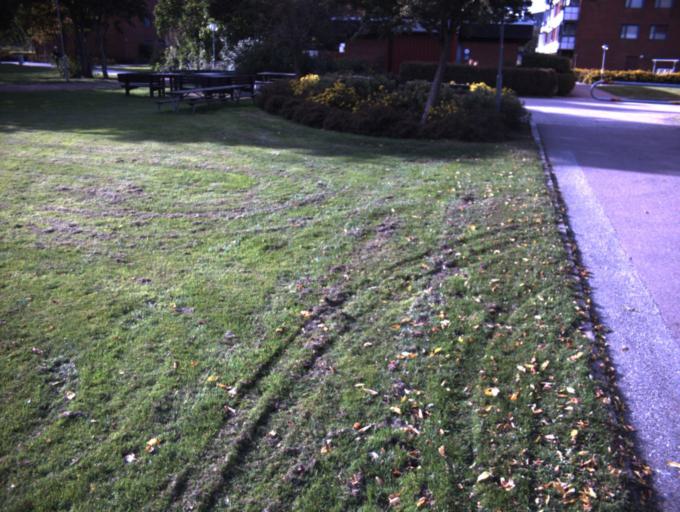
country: SE
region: Skane
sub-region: Helsingborg
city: Helsingborg
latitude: 56.0613
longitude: 12.7142
